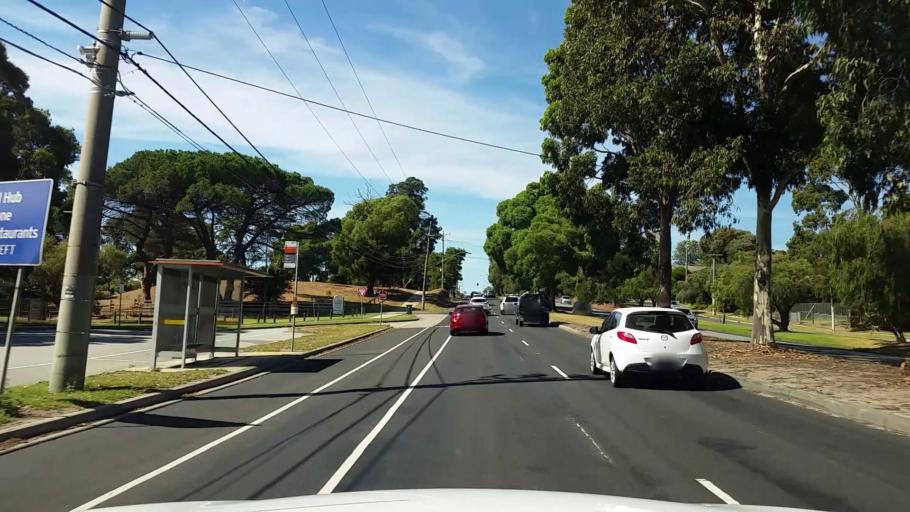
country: AU
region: Victoria
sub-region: Frankston
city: Langwarrin
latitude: -38.1532
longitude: 145.1591
